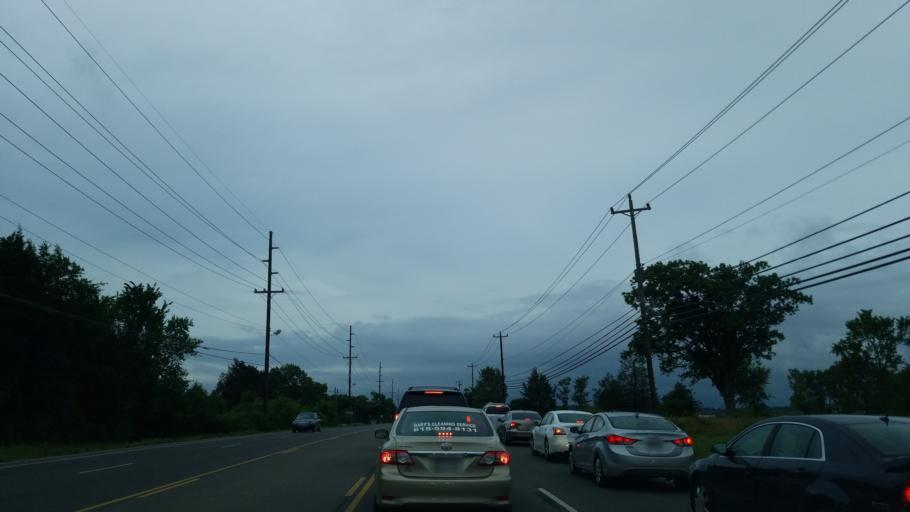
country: US
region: Tennessee
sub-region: Rutherford County
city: La Vergne
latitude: 36.0333
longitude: -86.5961
